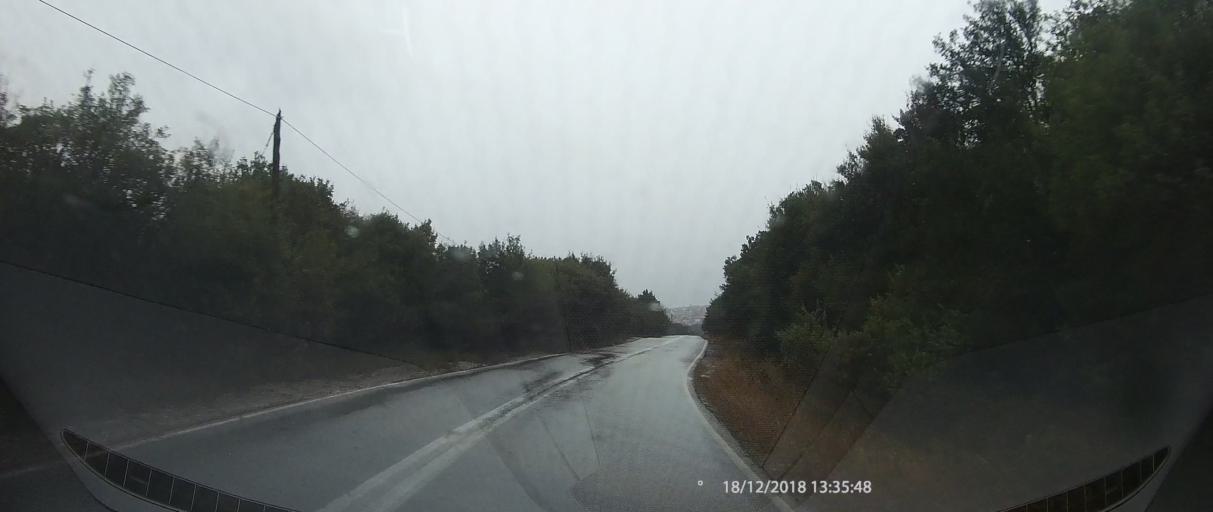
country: GR
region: Central Macedonia
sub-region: Nomos Pierias
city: Litochoro
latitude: 40.1149
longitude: 22.4898
